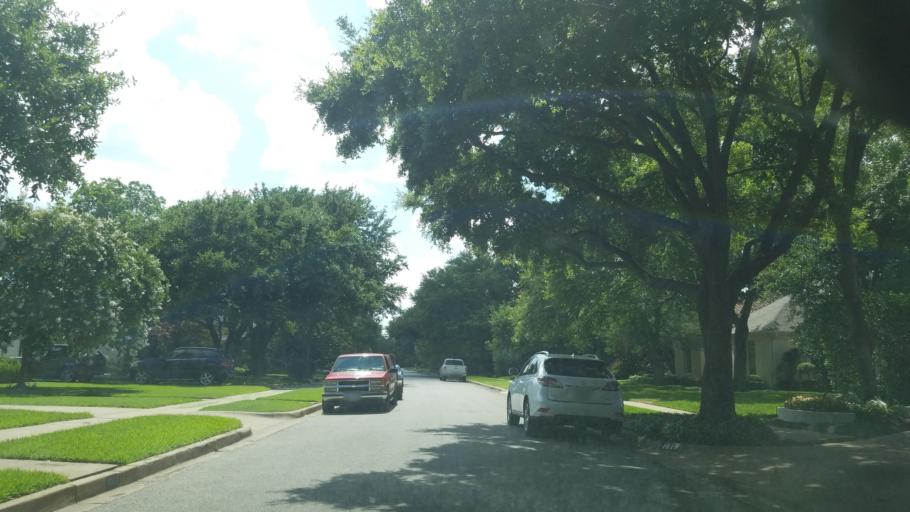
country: US
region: Texas
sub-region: Dallas County
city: Highland Park
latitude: 32.8314
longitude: -96.8165
